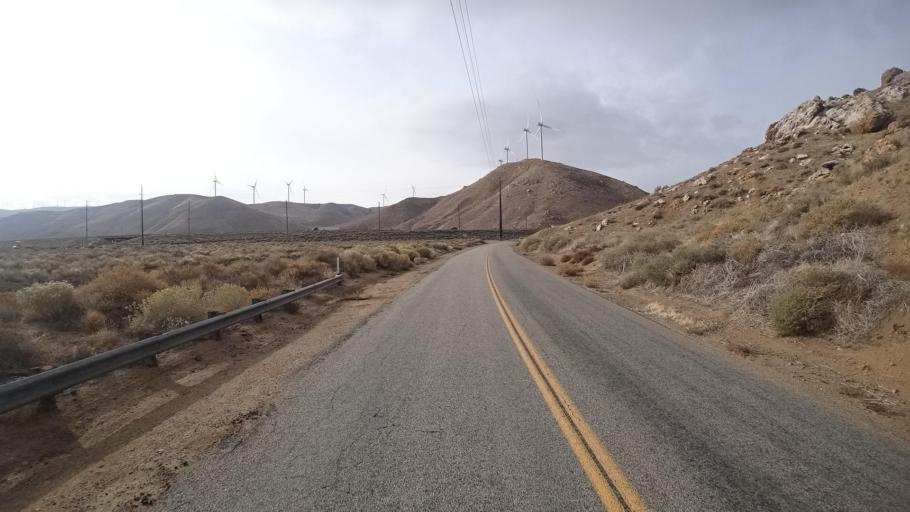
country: US
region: California
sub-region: Kern County
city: Tehachapi
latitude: 35.1127
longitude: -118.3240
